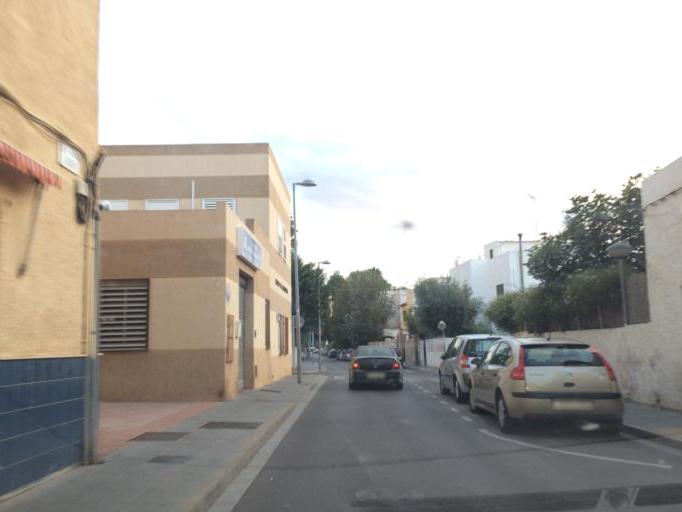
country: ES
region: Andalusia
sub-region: Provincia de Almeria
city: Almeria
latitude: 36.8337
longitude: -2.4512
